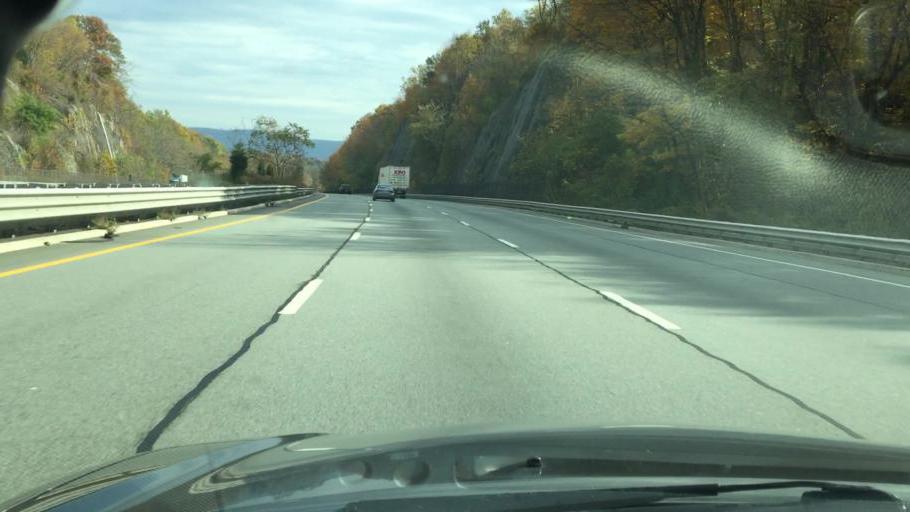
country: US
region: New Jersey
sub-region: Warren County
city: Hackettstown
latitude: 40.9293
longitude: -74.8952
